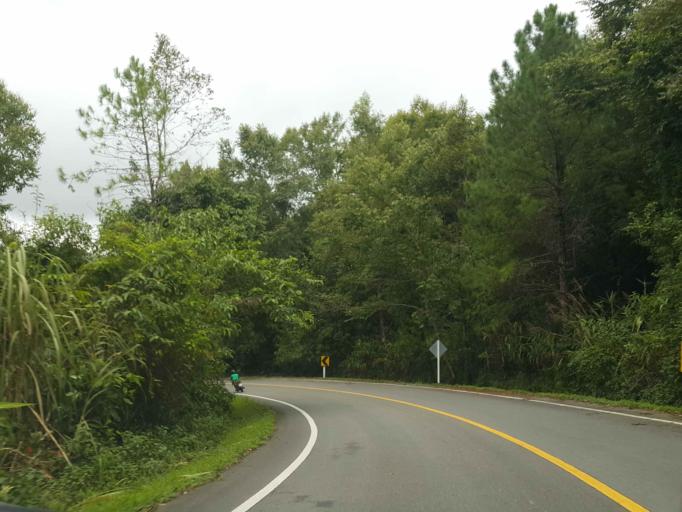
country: TH
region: Chiang Mai
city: Mae Chaem
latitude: 18.5352
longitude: 98.4933
